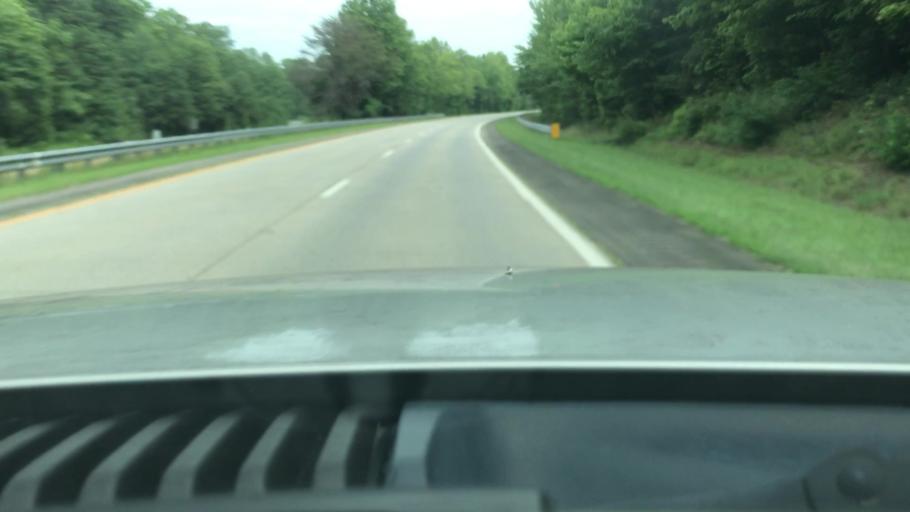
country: US
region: North Carolina
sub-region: Surry County
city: Elkin
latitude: 36.2663
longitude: -80.8288
